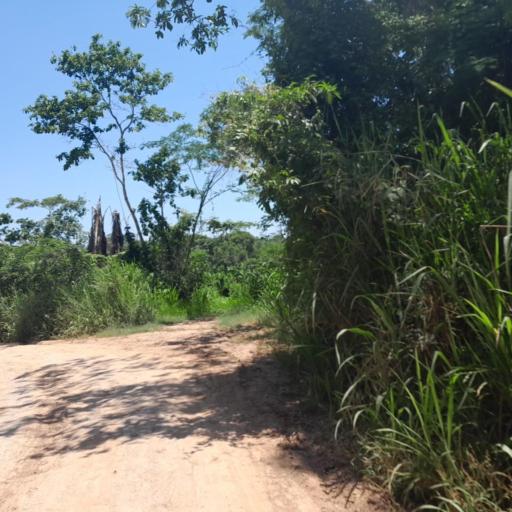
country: PE
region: Ucayali
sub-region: Provincia de Coronel Portillo
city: Puerto Callao
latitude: -8.2673
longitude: -74.6446
